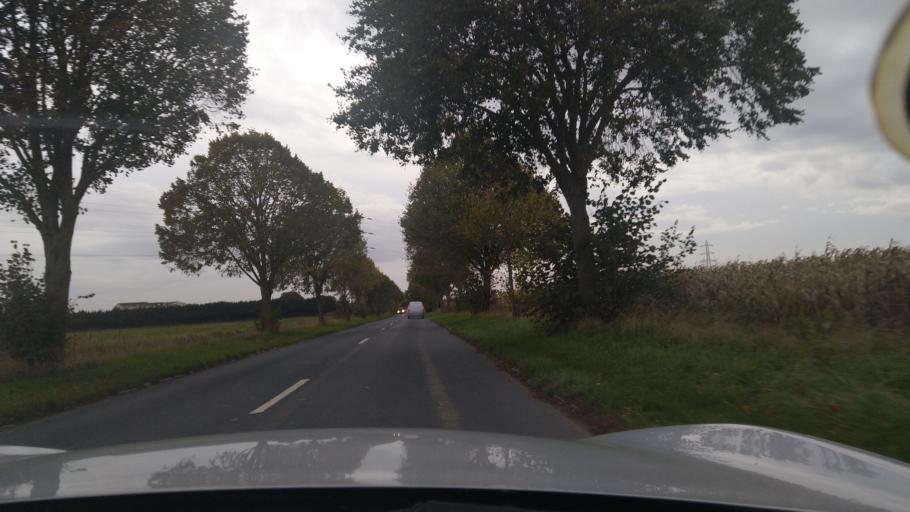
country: FR
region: Ile-de-France
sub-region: Departement de Seine-Saint-Denis
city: Villepinte
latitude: 48.9740
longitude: 2.5539
